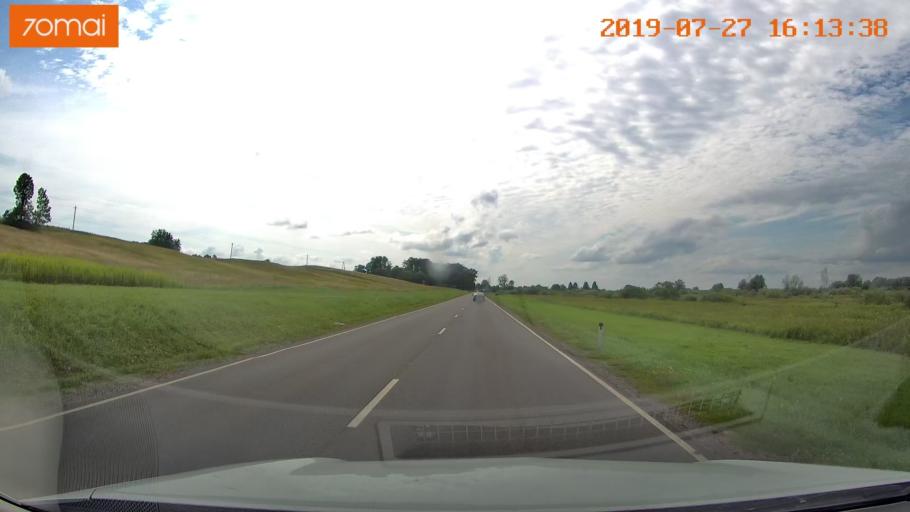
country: RU
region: Kaliningrad
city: Chernyakhovsk
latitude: 54.6285
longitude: 21.6349
